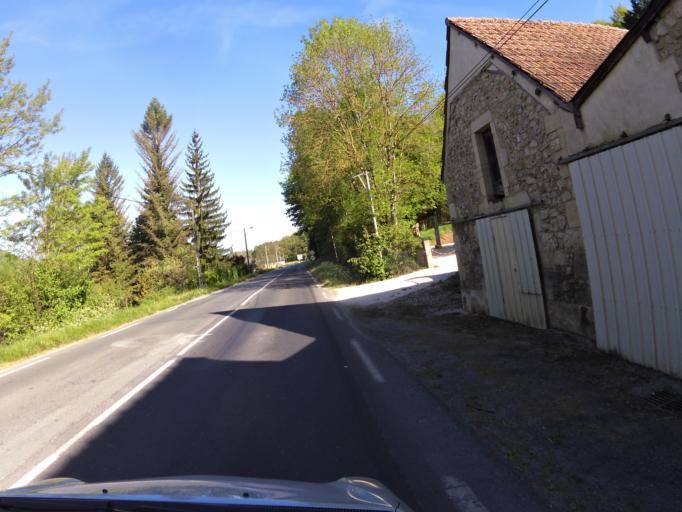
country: FR
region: Aquitaine
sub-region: Departement de la Dordogne
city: Montignac
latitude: 45.1362
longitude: 1.2025
